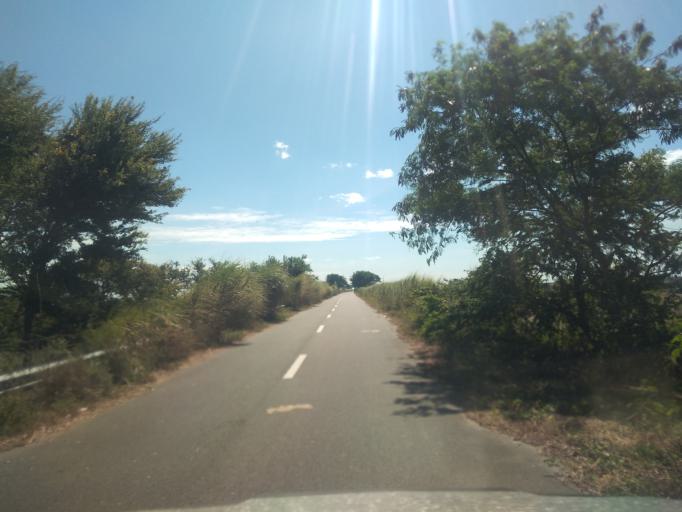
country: PH
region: Central Luzon
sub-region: Province of Pampanga
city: San Basilio
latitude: 15.0401
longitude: 120.5946
